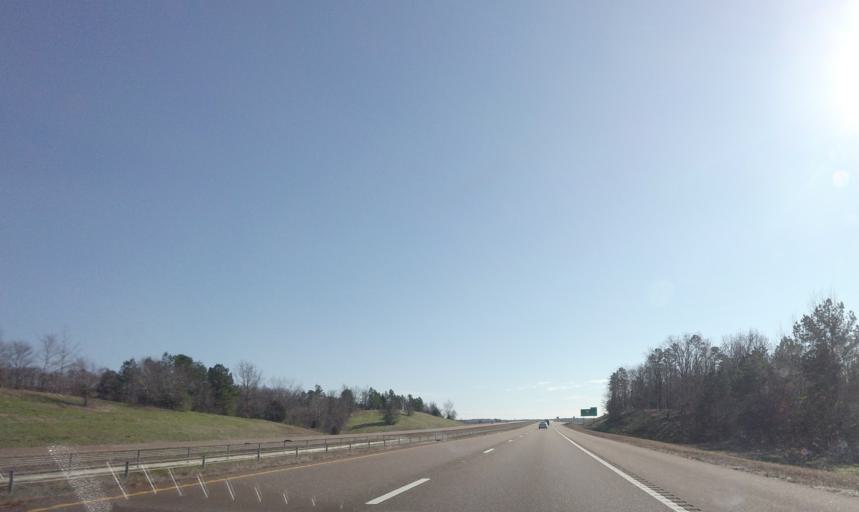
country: US
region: Mississippi
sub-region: Benton County
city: Ashland
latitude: 34.6245
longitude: -89.2064
